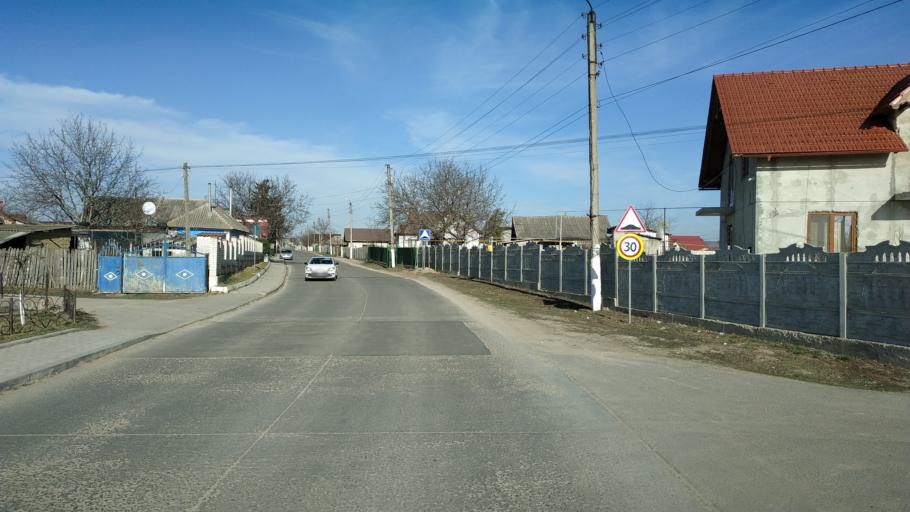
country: MD
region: Chisinau
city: Vatra
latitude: 47.0098
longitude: 28.6649
